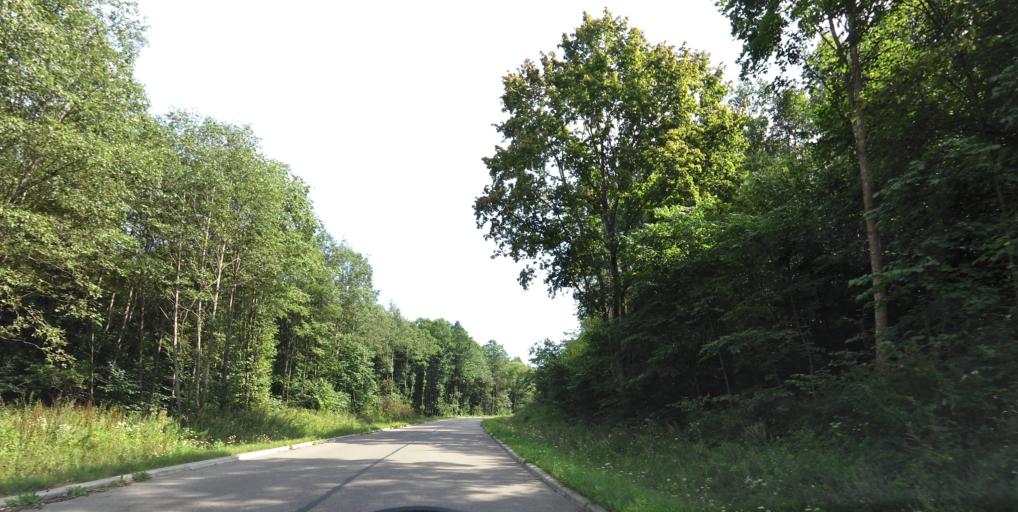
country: LT
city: Grigiskes
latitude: 54.7282
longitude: 25.0680
